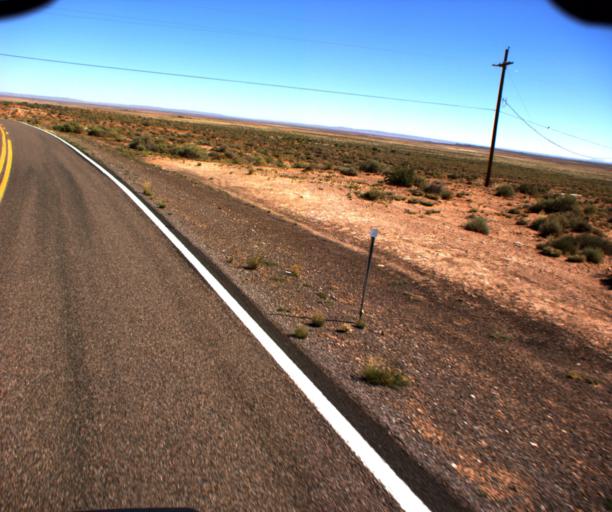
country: US
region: Arizona
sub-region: Coconino County
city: LeChee
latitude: 35.1238
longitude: -110.8735
